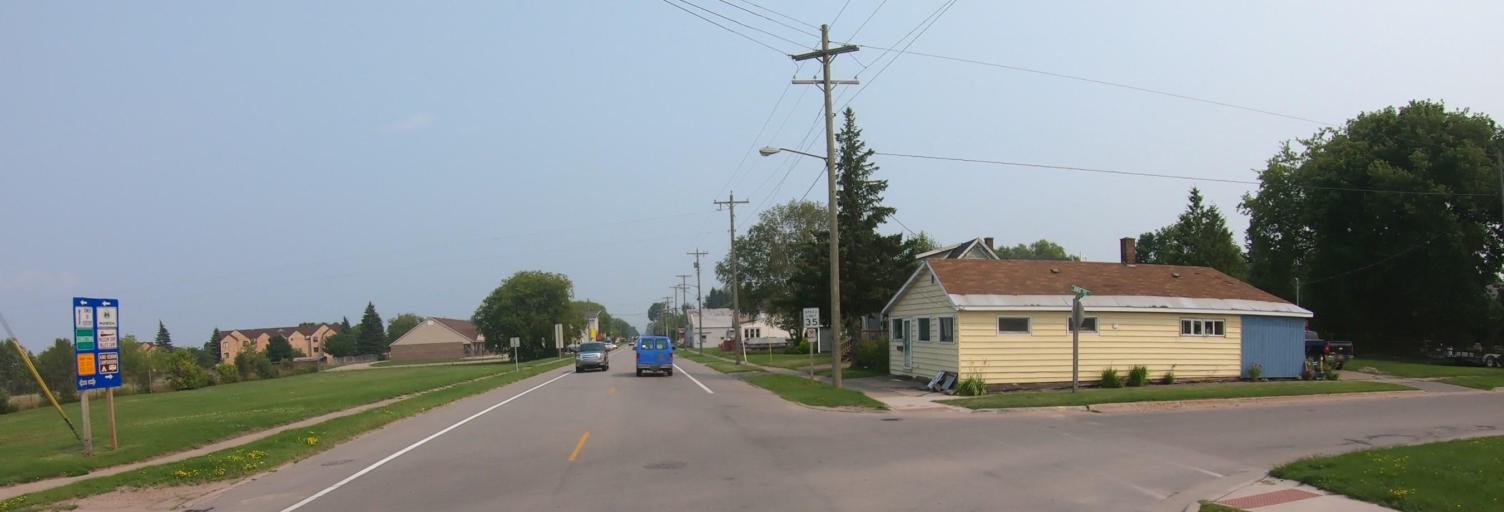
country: US
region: Michigan
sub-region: Chippewa County
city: Sault Ste. Marie
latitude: 46.4941
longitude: -84.3275
